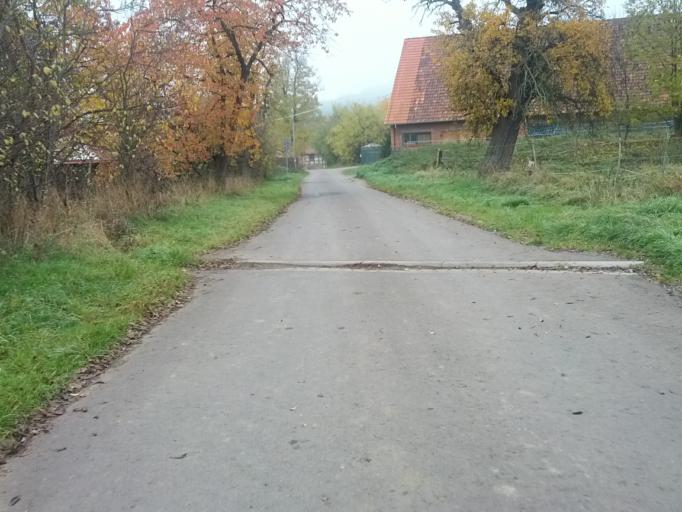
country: DE
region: Thuringia
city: Eisenach
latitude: 50.9743
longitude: 10.3719
